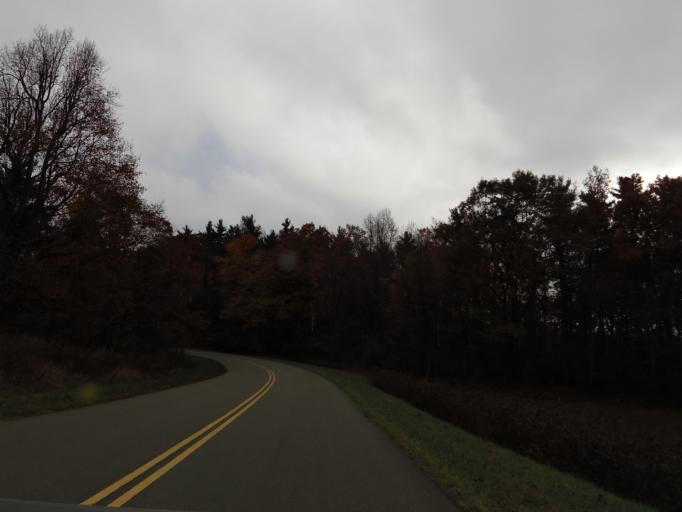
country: US
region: North Carolina
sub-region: Ashe County
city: Jefferson
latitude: 36.3322
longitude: -81.3745
